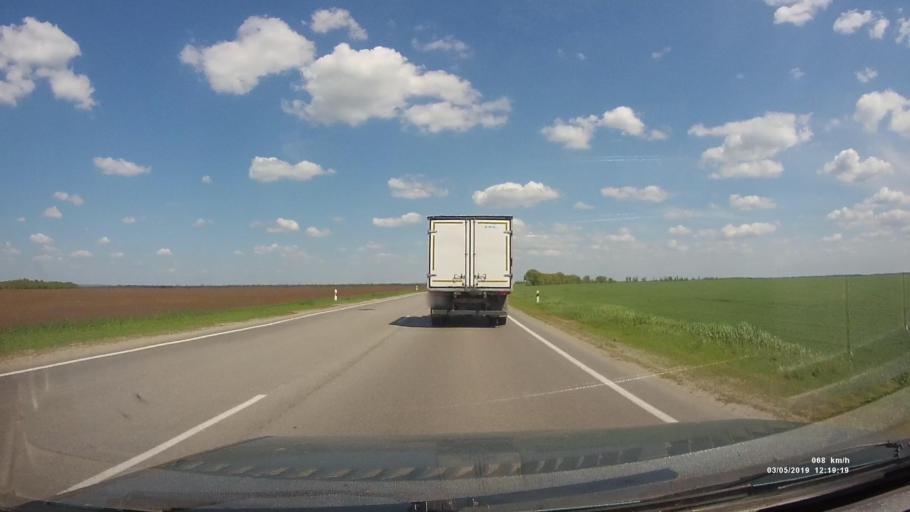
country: RU
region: Rostov
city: Melikhovskaya
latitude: 47.3994
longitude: 40.6062
